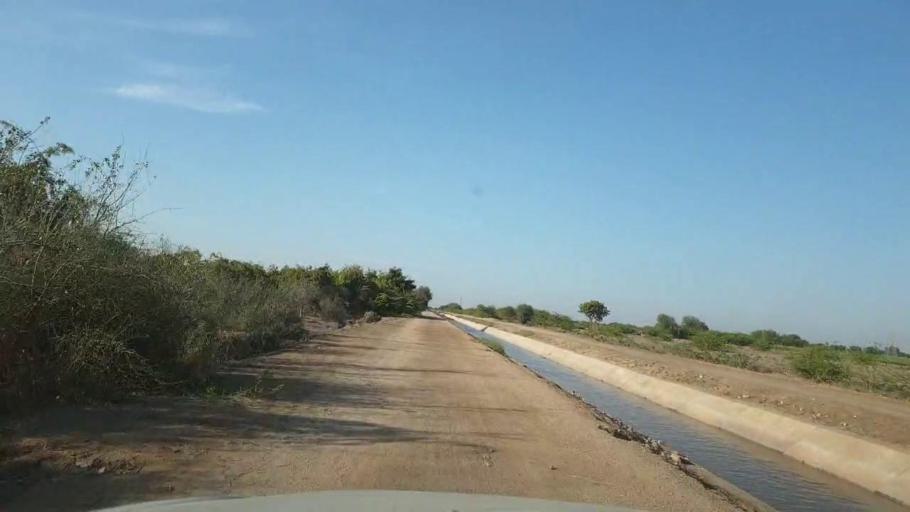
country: PK
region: Sindh
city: Kunri
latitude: 25.0921
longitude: 69.4287
